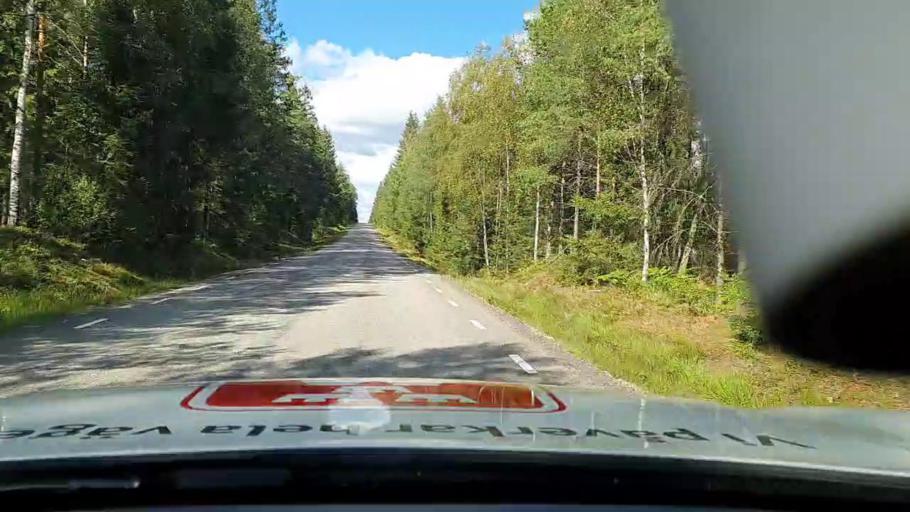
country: SE
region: Vaestra Goetaland
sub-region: Marks Kommun
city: Fritsla
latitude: 57.3822
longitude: 12.8581
